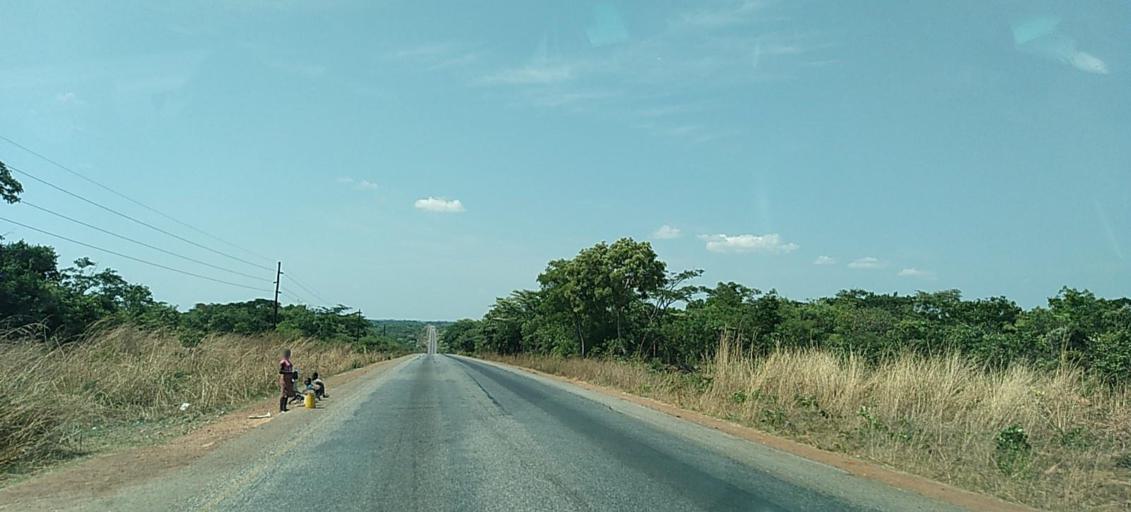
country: ZM
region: Central
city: Kapiri Mposhi
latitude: -13.5412
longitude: 28.6447
